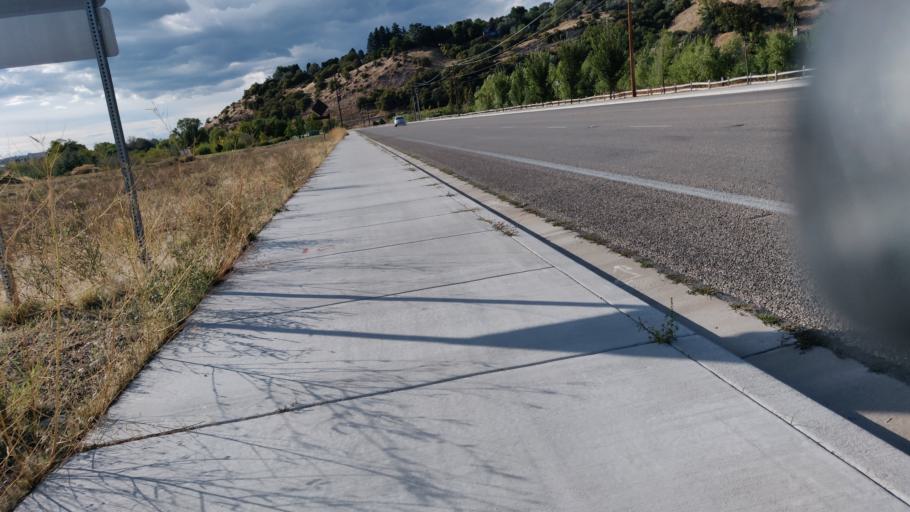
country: US
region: Idaho
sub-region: Ada County
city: Boise
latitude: 43.5771
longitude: -116.1418
